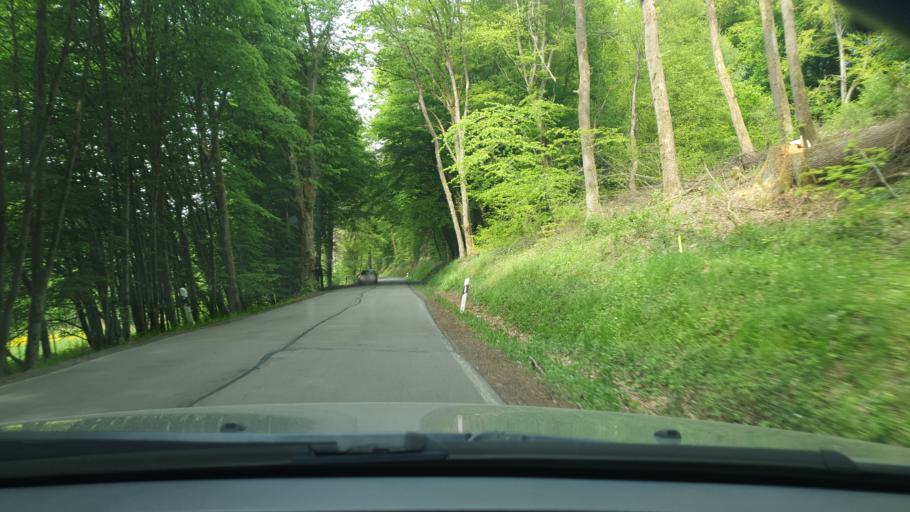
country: DE
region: Rheinland-Pfalz
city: Gerhardsbrunn
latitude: 49.3360
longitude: 7.5255
